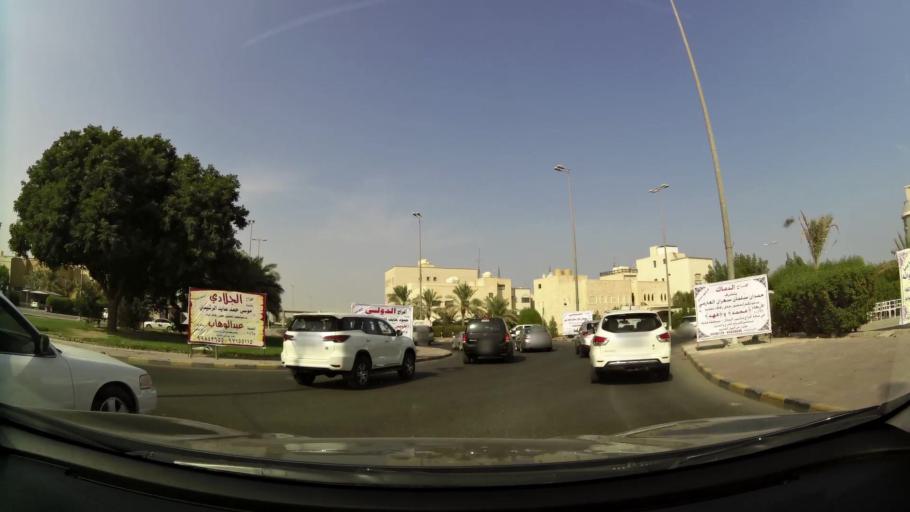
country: KW
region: Al Ahmadi
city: Ar Riqqah
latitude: 29.1600
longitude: 48.0857
